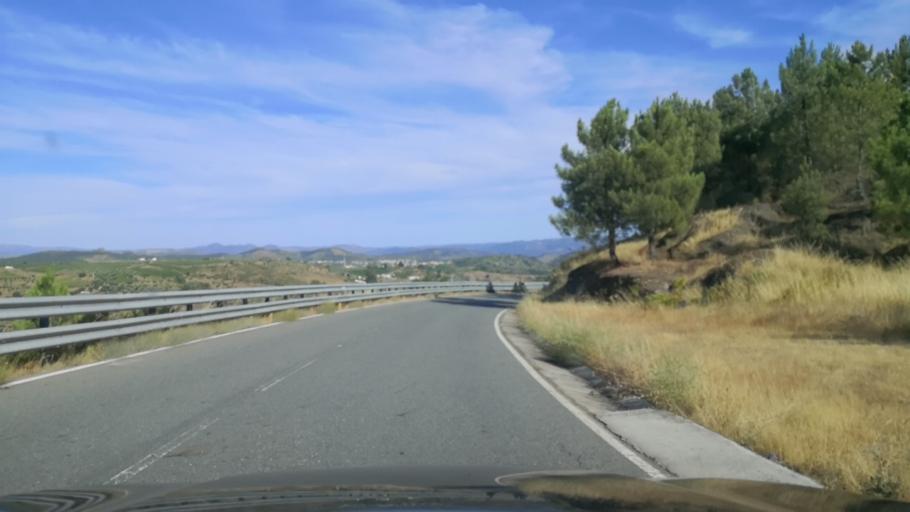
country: PT
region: Vila Real
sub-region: Murca
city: Murca
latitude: 41.4065
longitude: -7.4769
